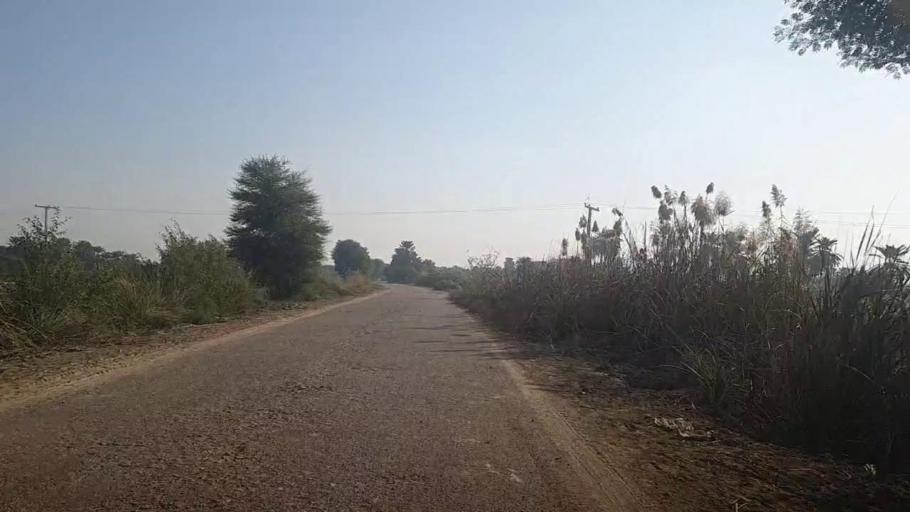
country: PK
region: Sindh
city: Bozdar
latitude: 27.2594
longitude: 68.6758
